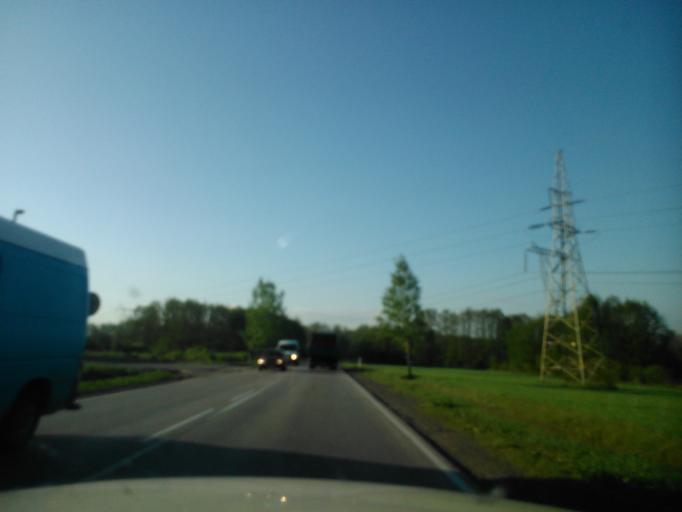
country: PL
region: Masovian Voivodeship
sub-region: Powiat sochaczewski
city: Mlodzieszyn
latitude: 52.3348
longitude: 20.2161
